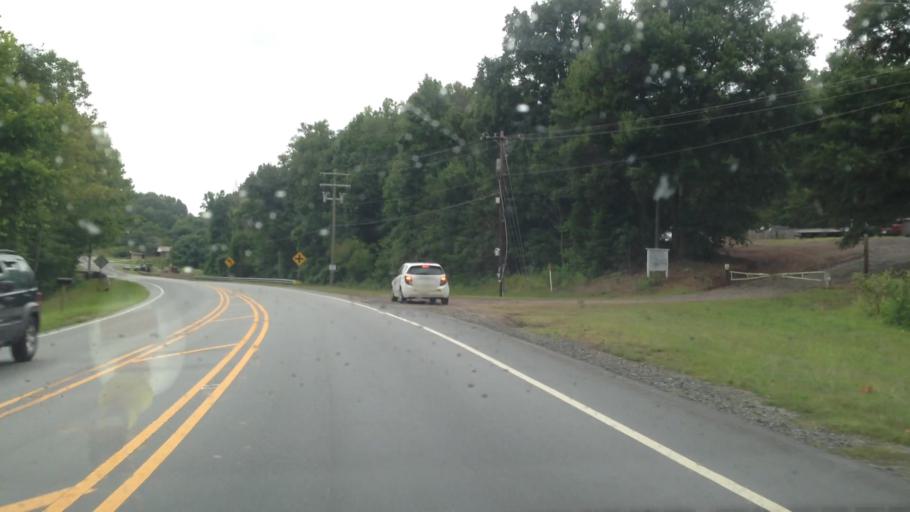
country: US
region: North Carolina
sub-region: Rockingham County
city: Mayodan
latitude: 36.4082
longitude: -79.9870
